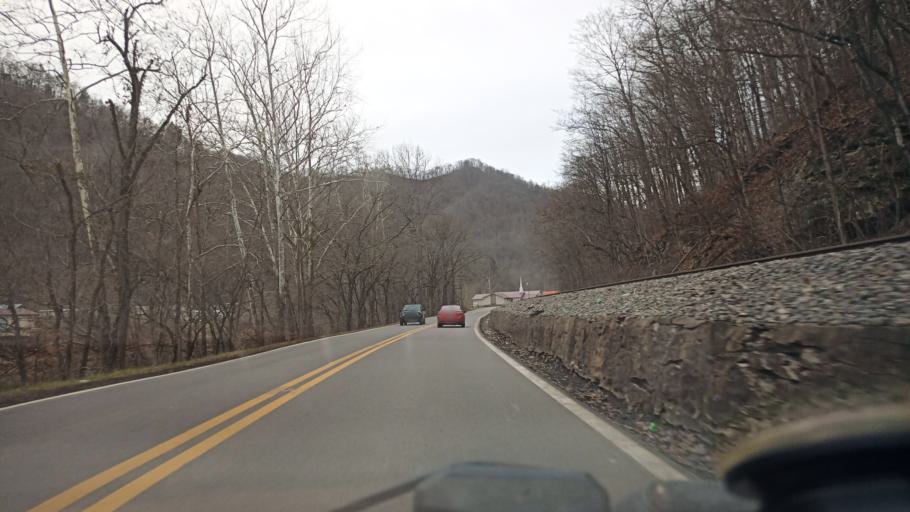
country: US
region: West Virginia
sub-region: Logan County
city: Mallory
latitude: 37.7240
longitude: -81.8736
